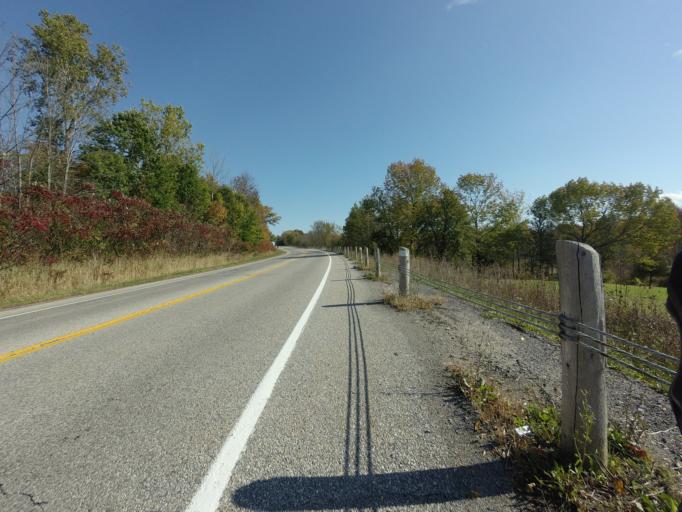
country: CA
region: Ontario
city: Kingston
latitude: 44.2149
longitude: -76.6833
